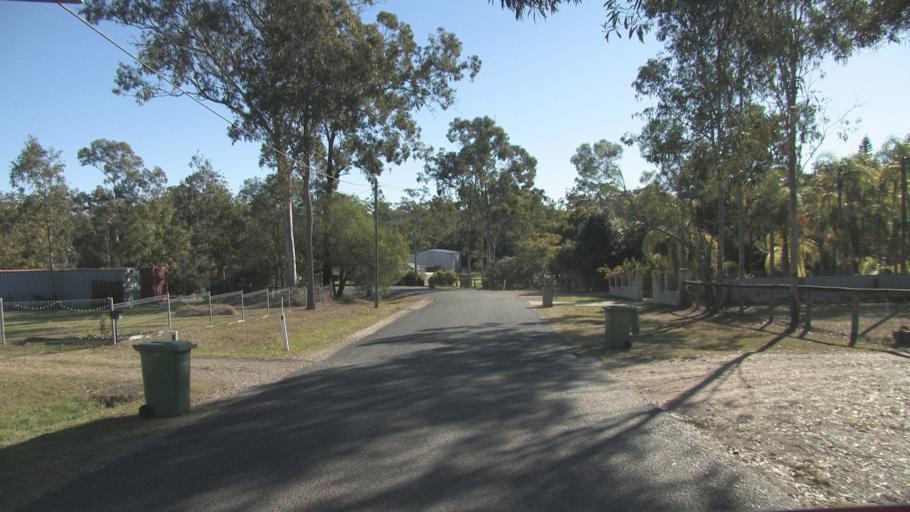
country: AU
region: Queensland
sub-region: Logan
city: Park Ridge South
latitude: -27.7405
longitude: 153.0134
